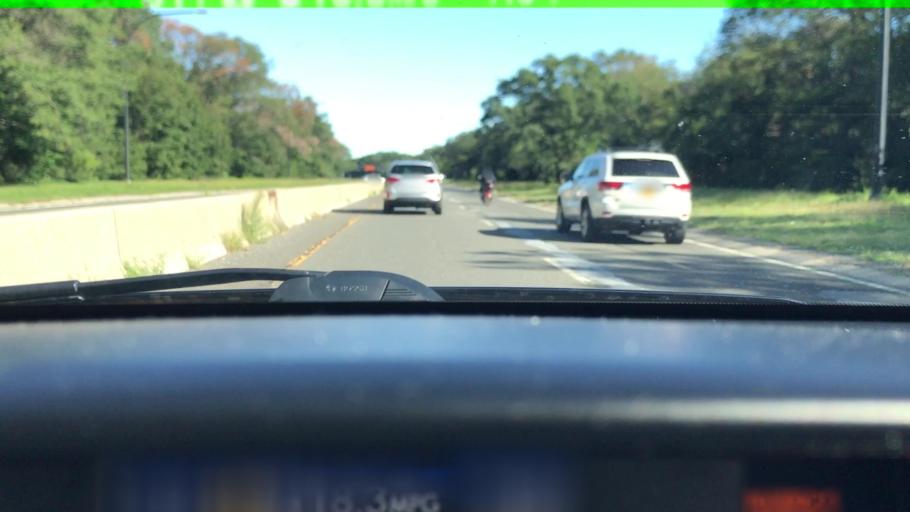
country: US
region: New York
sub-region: Nassau County
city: Salisbury
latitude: 40.7370
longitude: -73.5437
